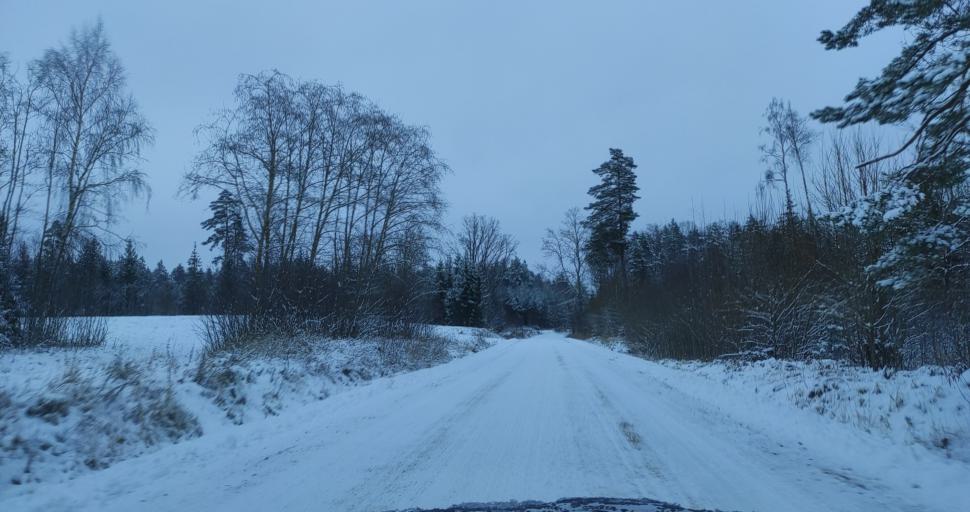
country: LV
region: Kuldigas Rajons
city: Kuldiga
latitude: 56.9515
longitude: 21.7624
